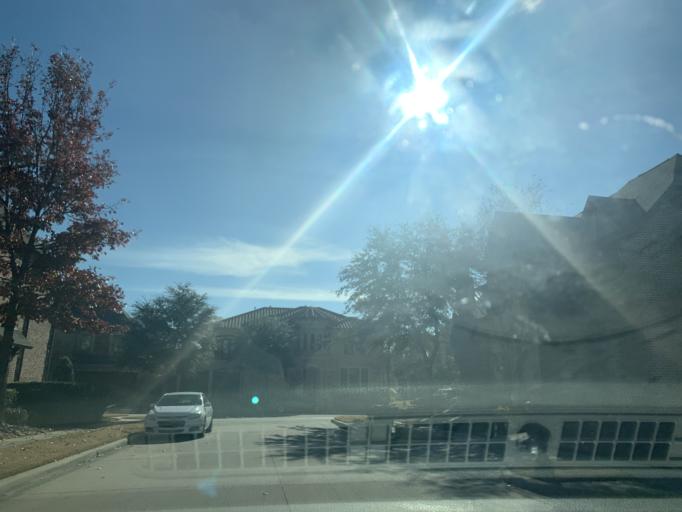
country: US
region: Texas
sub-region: Denton County
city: The Colony
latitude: 33.0595
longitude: -96.8202
